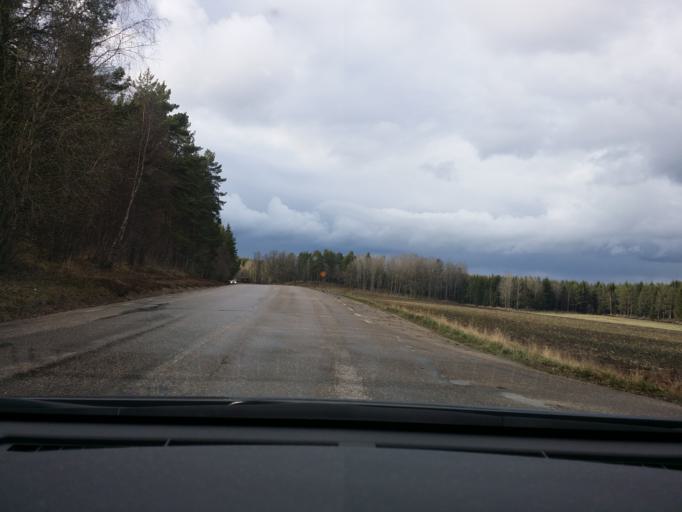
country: SE
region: Soedermanland
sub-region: Eskilstuna Kommun
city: Arla
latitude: 59.3074
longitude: 16.6836
